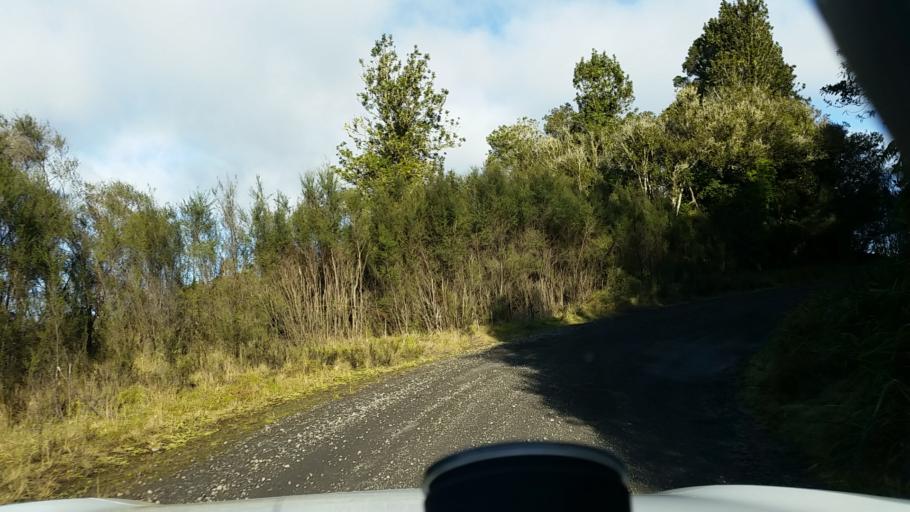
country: NZ
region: Taranaki
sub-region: South Taranaki District
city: Eltham
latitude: -39.4071
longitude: 174.5556
